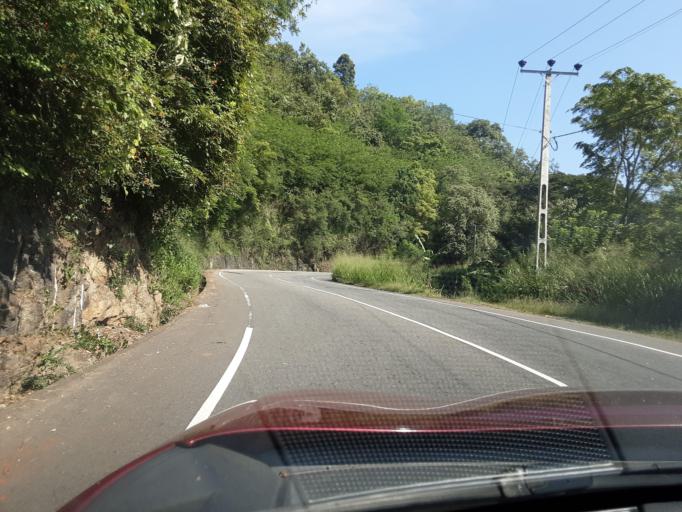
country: LK
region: Uva
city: Badulla
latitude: 7.0424
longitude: 81.0616
